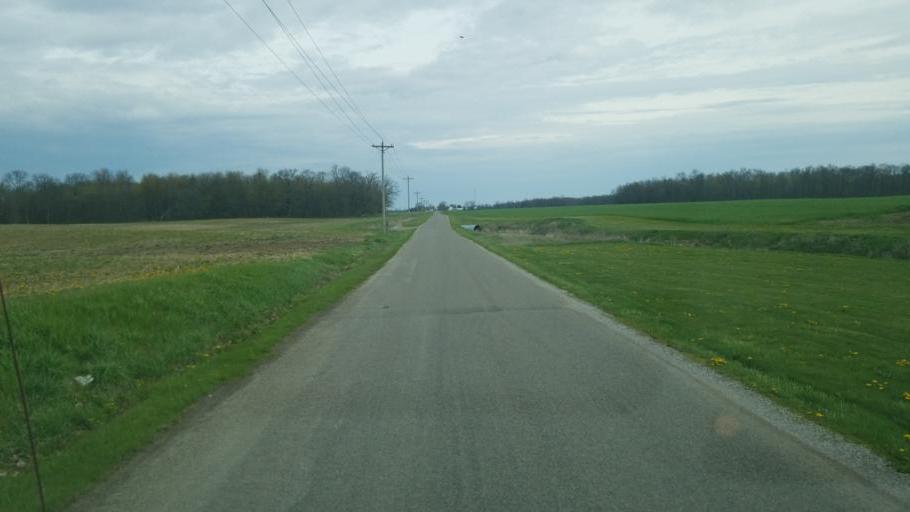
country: US
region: Ohio
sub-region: Marion County
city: Marion
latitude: 40.6018
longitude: -82.9909
